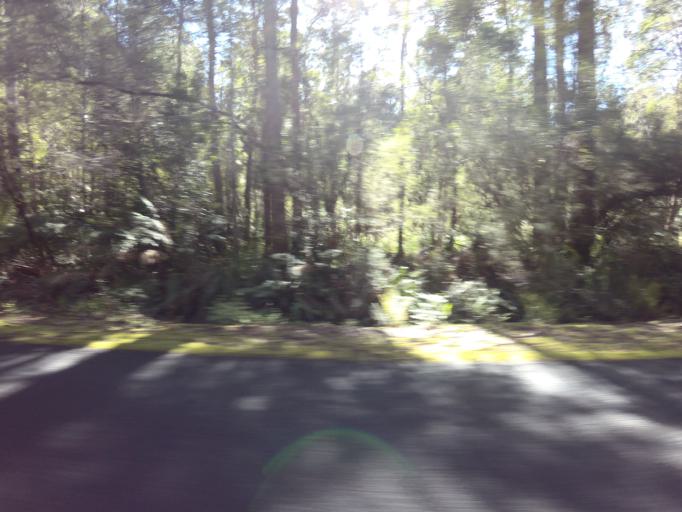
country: AU
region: Tasmania
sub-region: Derwent Valley
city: New Norfolk
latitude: -42.7532
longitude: 146.5237
